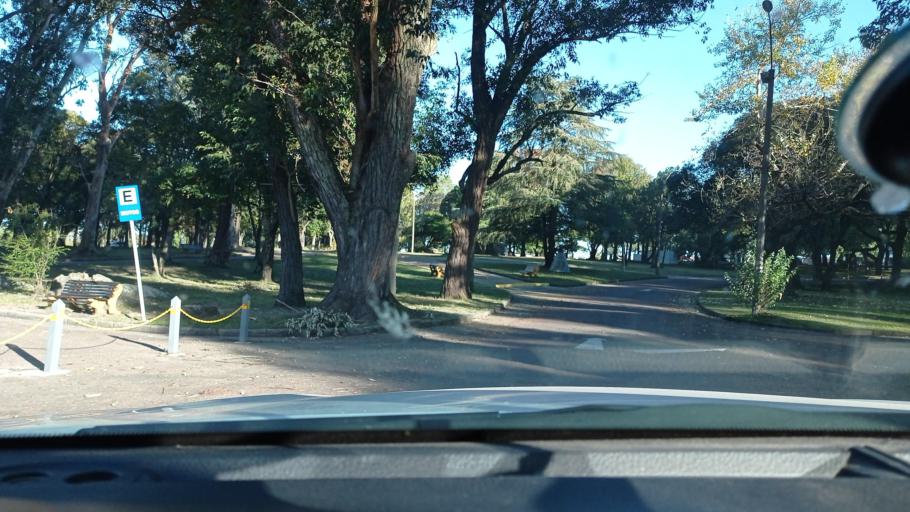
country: UY
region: Florida
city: Florida
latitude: -34.0984
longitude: -56.2057
